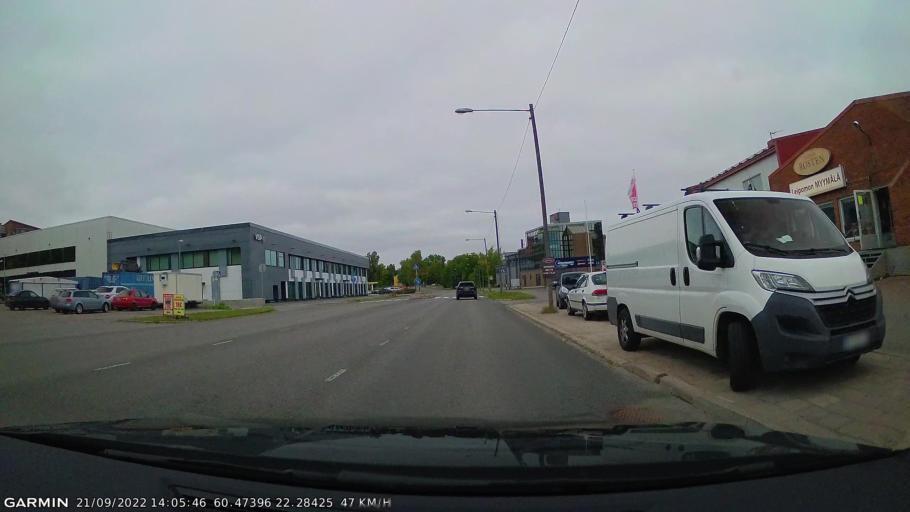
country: FI
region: Varsinais-Suomi
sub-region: Turku
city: Turku
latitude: 60.4741
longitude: 22.2840
